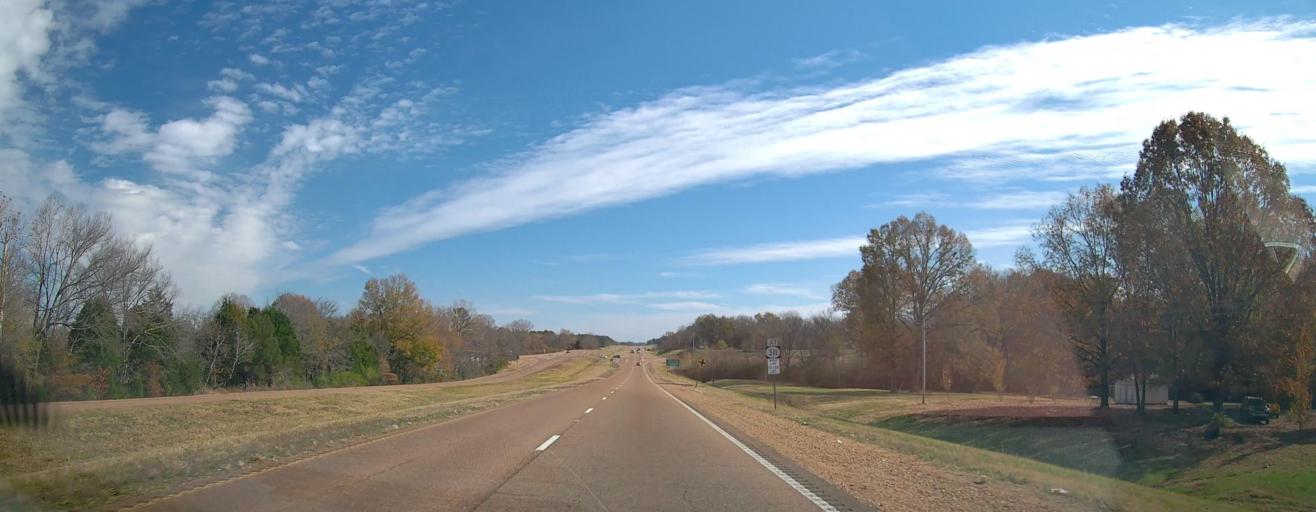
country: US
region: Tennessee
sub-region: Fayette County
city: Piperton
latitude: 34.9586
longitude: -89.5198
